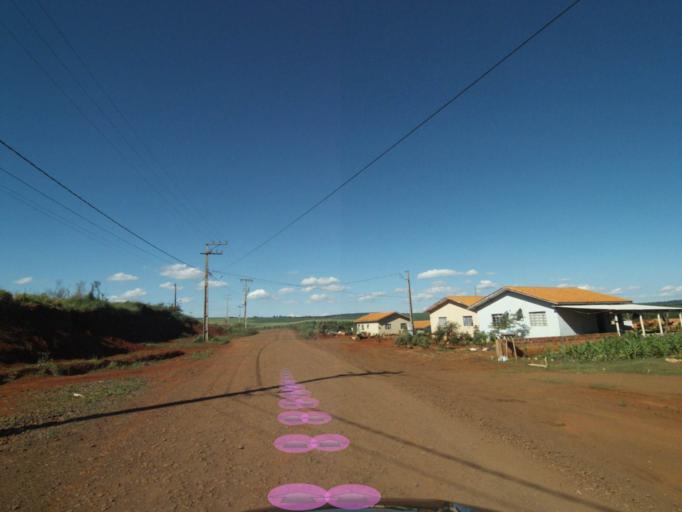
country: BR
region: Parana
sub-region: Coronel Vivida
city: Coronel Vivida
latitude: -26.1367
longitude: -52.3934
